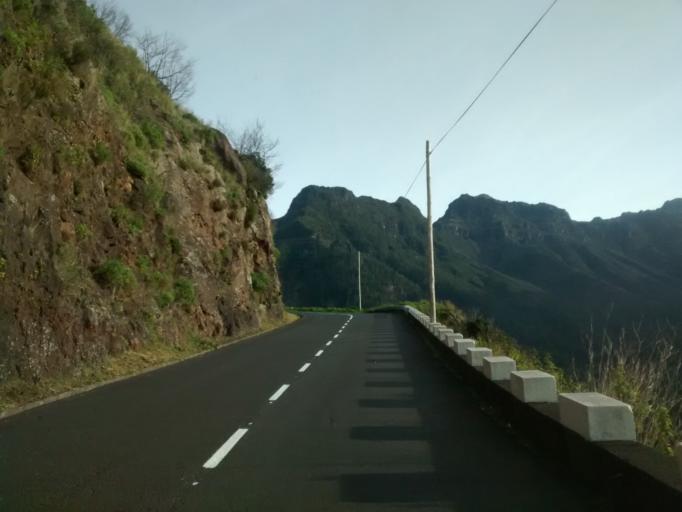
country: PT
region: Madeira
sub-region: Camara de Lobos
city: Curral das Freiras
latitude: 32.7373
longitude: -17.0250
